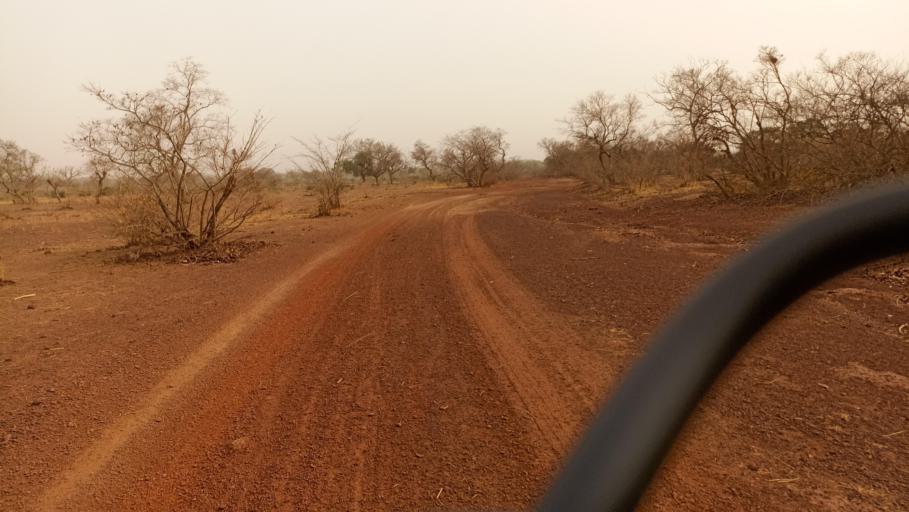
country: BF
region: Nord
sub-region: Province du Zondoma
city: Gourcy
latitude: 13.1534
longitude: -2.5953
